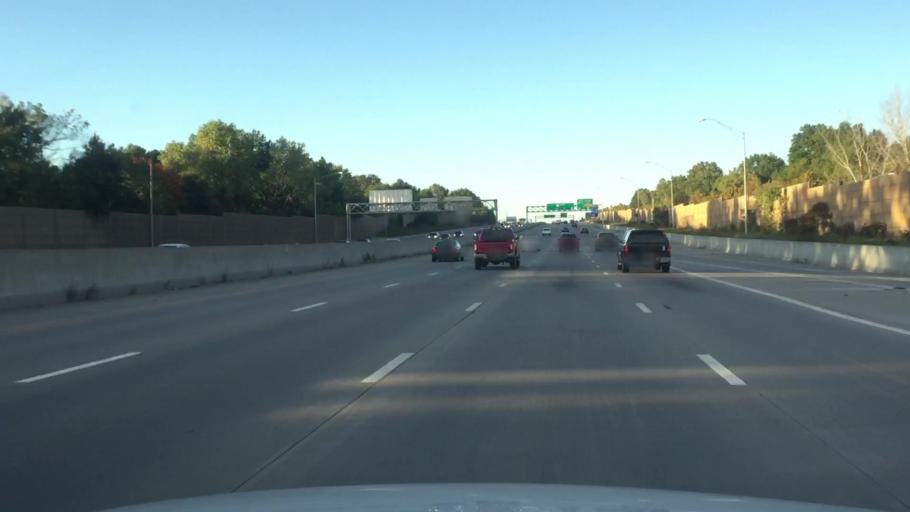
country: US
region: Kansas
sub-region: Johnson County
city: Lenexa
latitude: 38.9459
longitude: -94.7053
